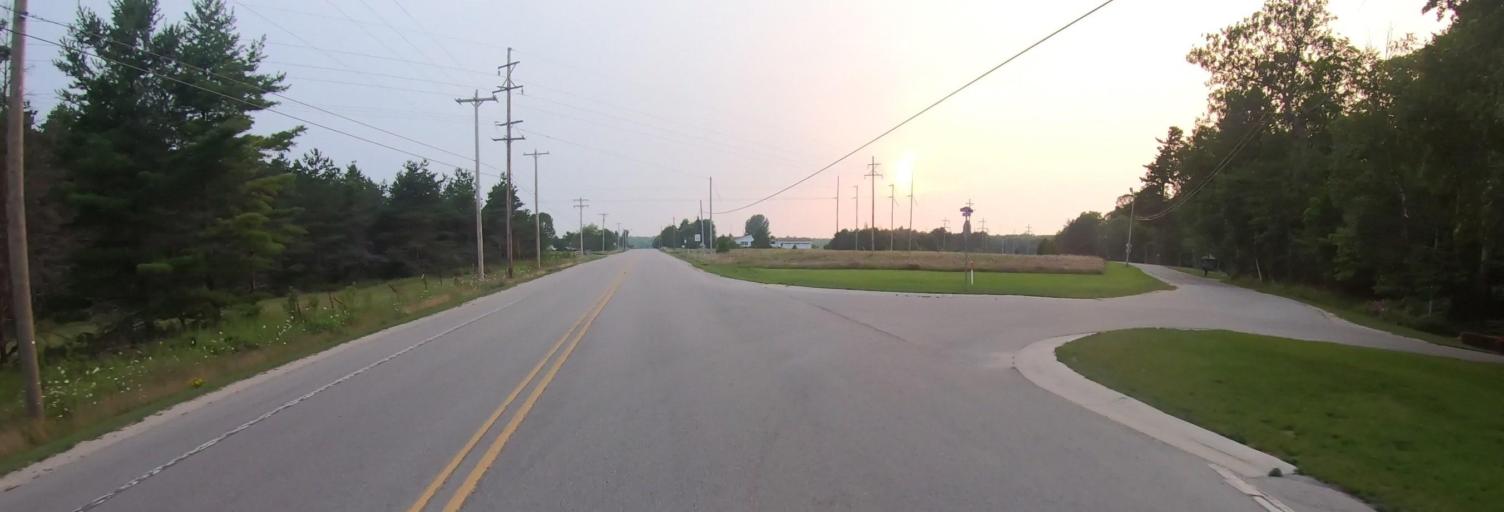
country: US
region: Michigan
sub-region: Mackinac County
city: Saint Ignace
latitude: 45.7818
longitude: -84.7604
